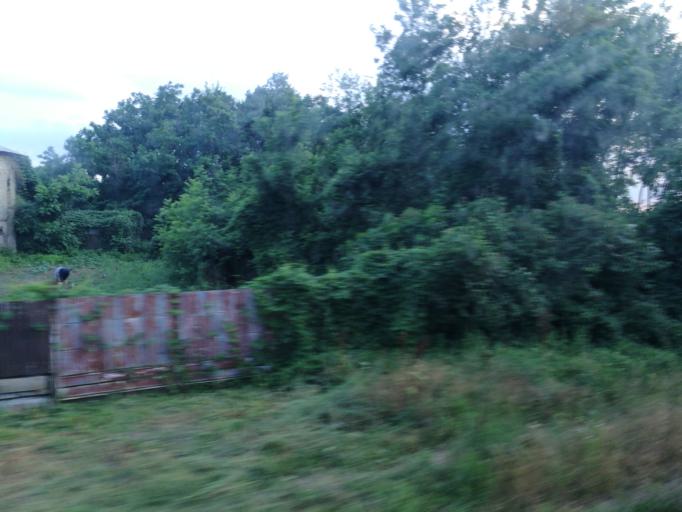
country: RO
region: Dambovita
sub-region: Comuna Branistea
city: Dambovicioara
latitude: 44.6660
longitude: 25.5399
